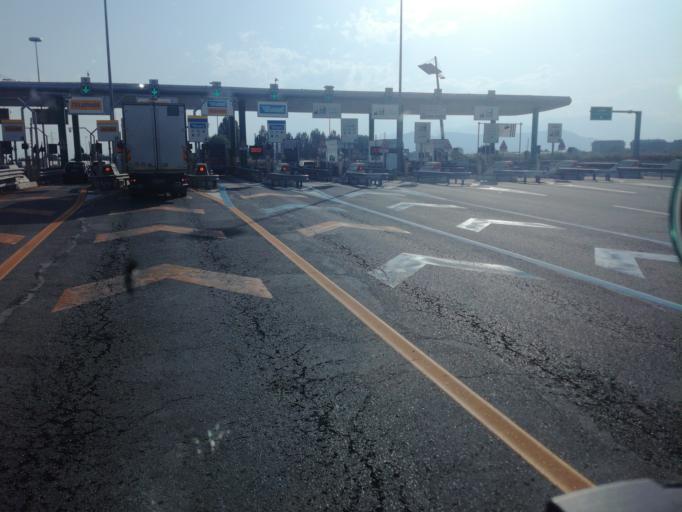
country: IT
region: Piedmont
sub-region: Provincia di Torino
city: Beinasco
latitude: 45.0143
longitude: 7.5873
